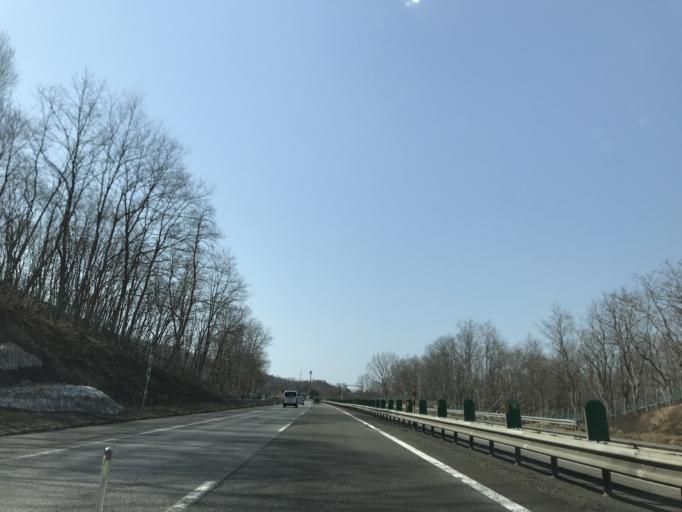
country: JP
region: Hokkaido
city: Bibai
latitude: 43.3180
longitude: 141.8843
